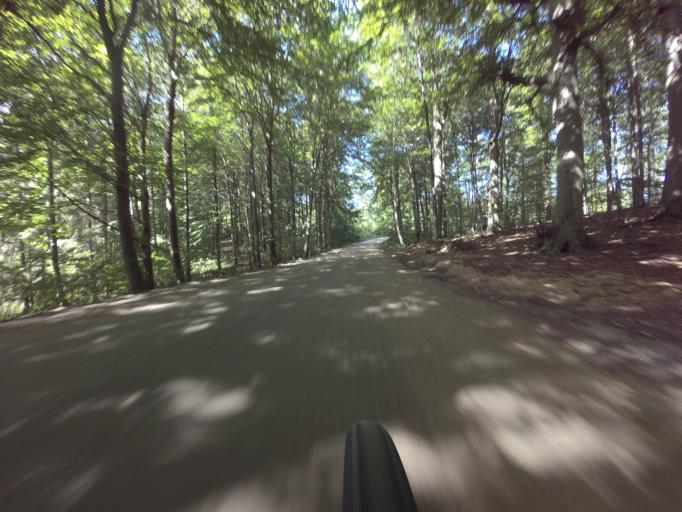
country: DK
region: Zealand
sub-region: Vordingborg Kommune
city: Stege
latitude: 54.9729
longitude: 12.5333
